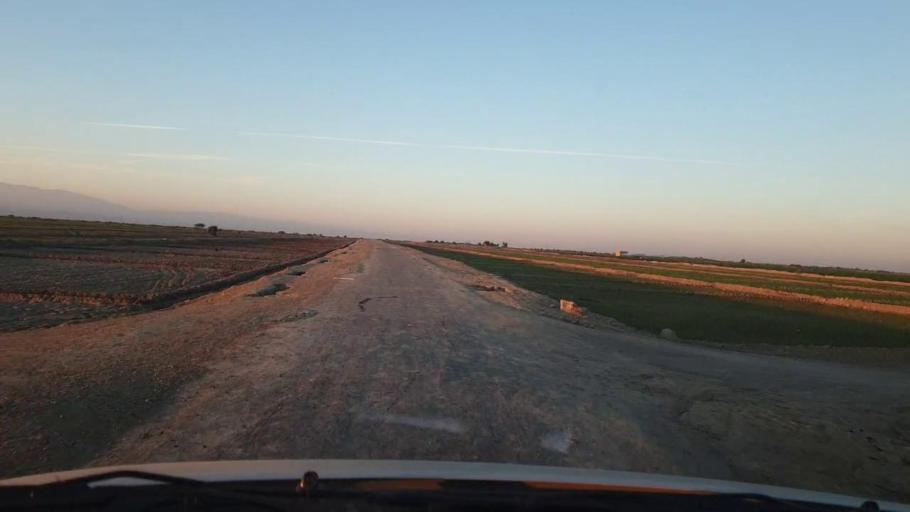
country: PK
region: Sindh
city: Johi
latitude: 26.8358
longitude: 67.4419
